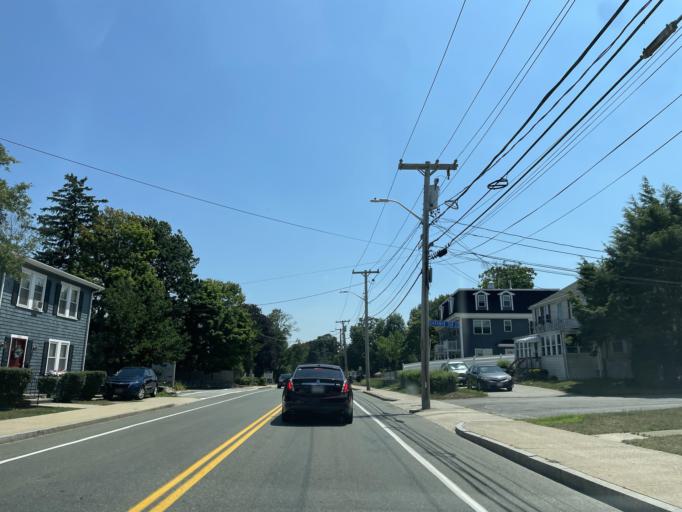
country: US
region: Massachusetts
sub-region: Norfolk County
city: Braintree
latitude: 42.2118
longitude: -71.0043
